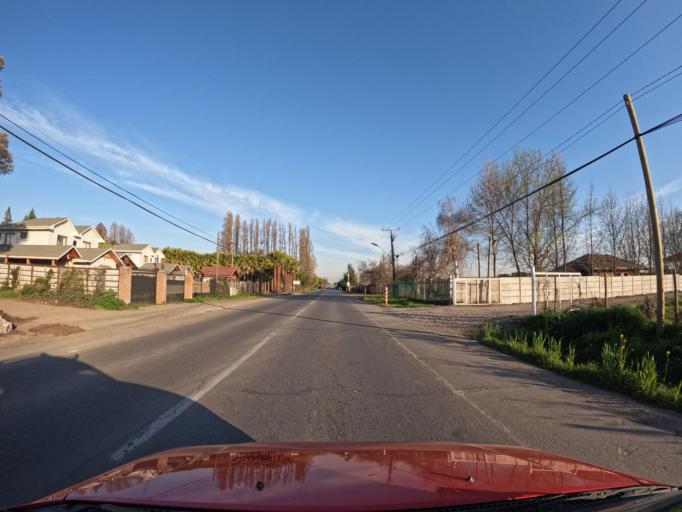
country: CL
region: Maule
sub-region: Provincia de Curico
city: Curico
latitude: -34.9515
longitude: -71.2565
